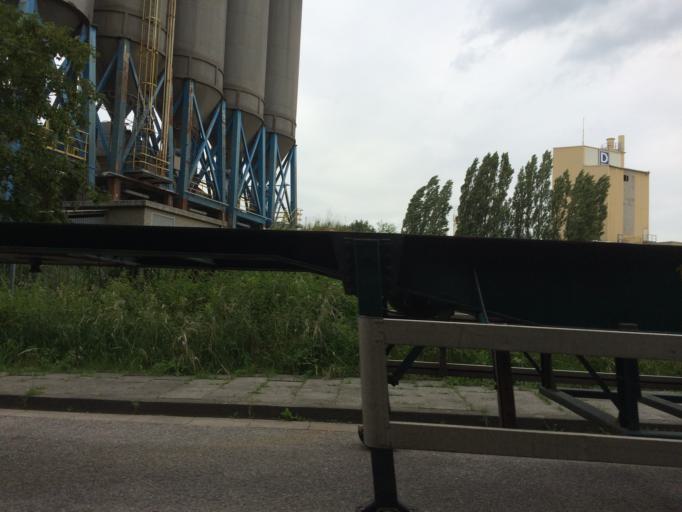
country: DE
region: North Rhine-Westphalia
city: Marl
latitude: 51.6830
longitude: 7.0685
